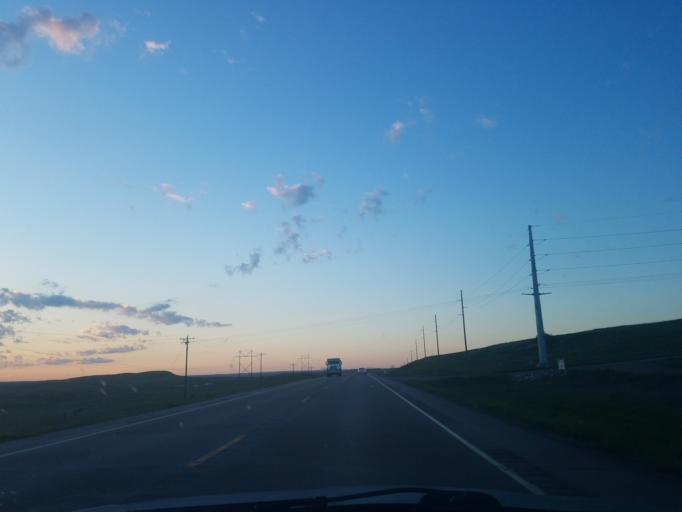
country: US
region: North Dakota
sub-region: McKenzie County
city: Watford City
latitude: 47.7025
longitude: -103.2834
